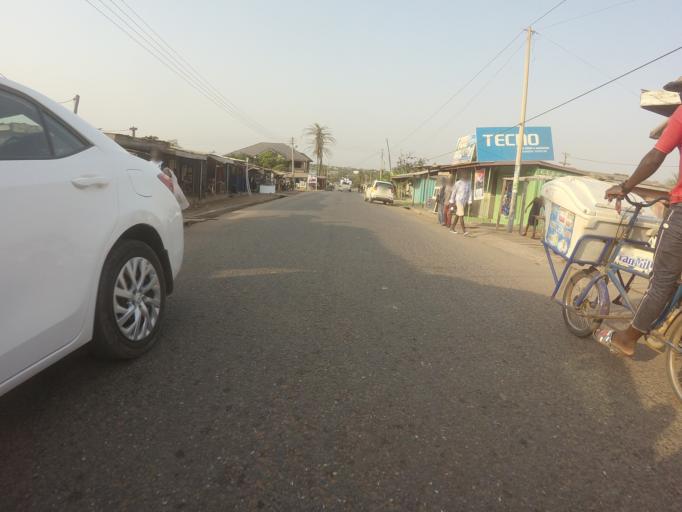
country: GH
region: Greater Accra
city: Nungua
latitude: 5.6149
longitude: -0.0478
